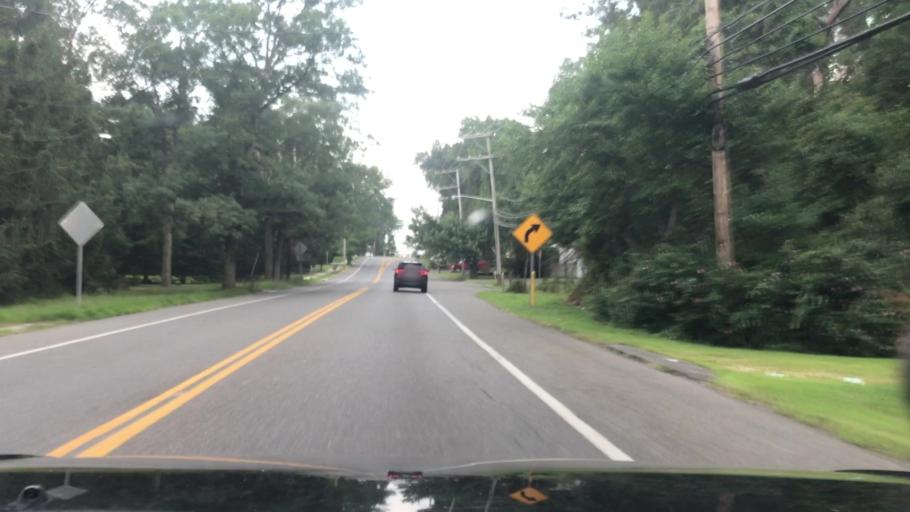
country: US
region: New Jersey
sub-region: Ocean County
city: Lakewood
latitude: 40.0878
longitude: -74.2673
